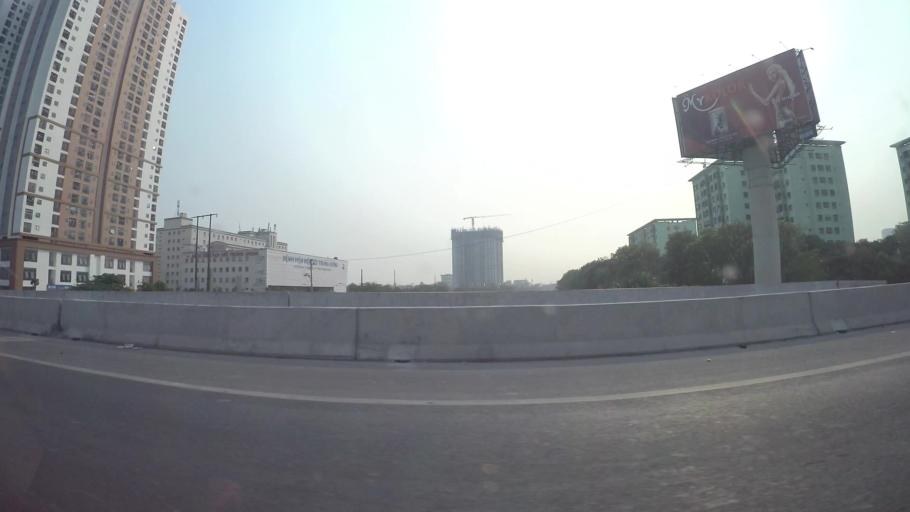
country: VN
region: Ha Noi
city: Van Dien
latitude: 20.9538
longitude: 105.8519
